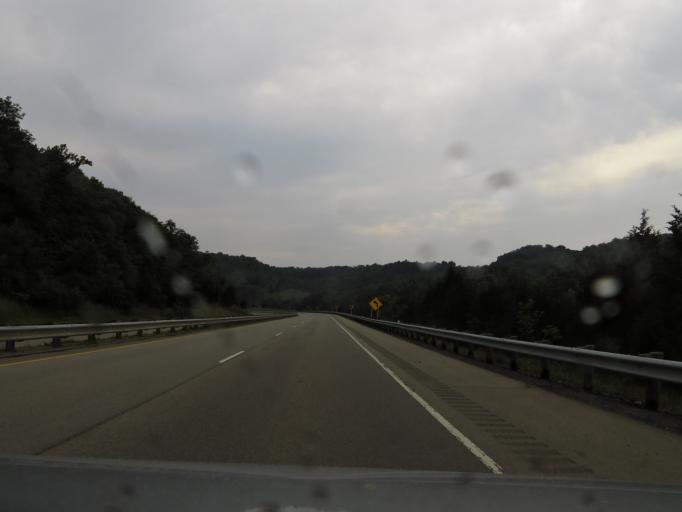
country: US
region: Ohio
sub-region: Brown County
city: Ripley
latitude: 38.7606
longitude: -83.8249
